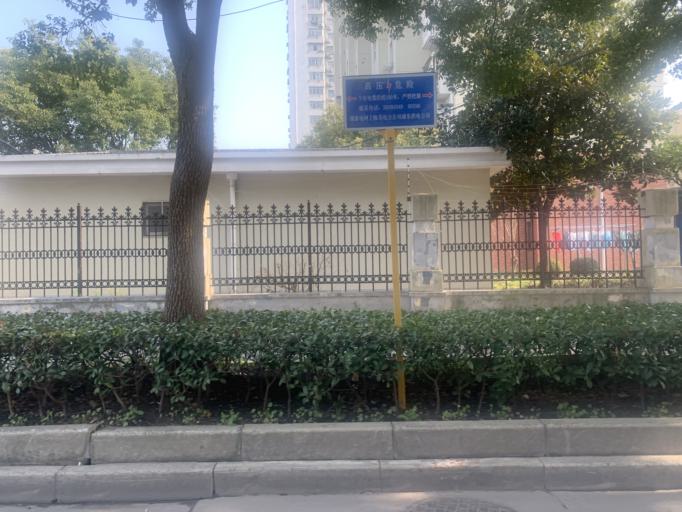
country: CN
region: Shanghai Shi
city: Huamu
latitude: 31.1858
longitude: 121.5146
